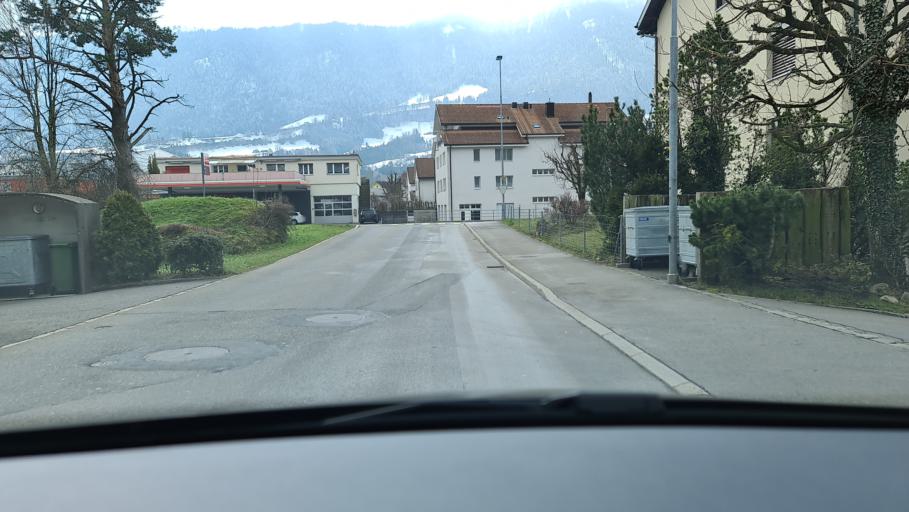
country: CH
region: Schwyz
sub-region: Bezirk Schwyz
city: Goldau
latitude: 47.0540
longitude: 8.5506
